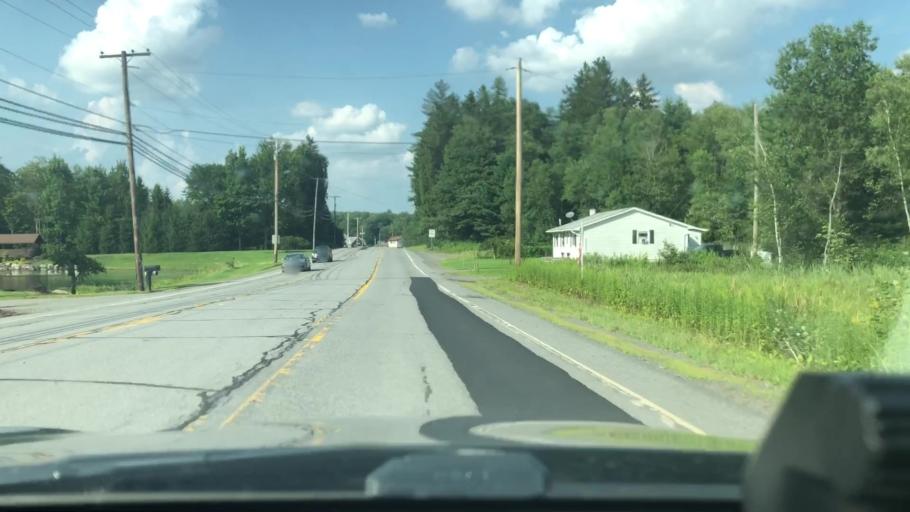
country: US
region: Pennsylvania
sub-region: Lackawanna County
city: Moscow
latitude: 41.2891
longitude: -75.5096
